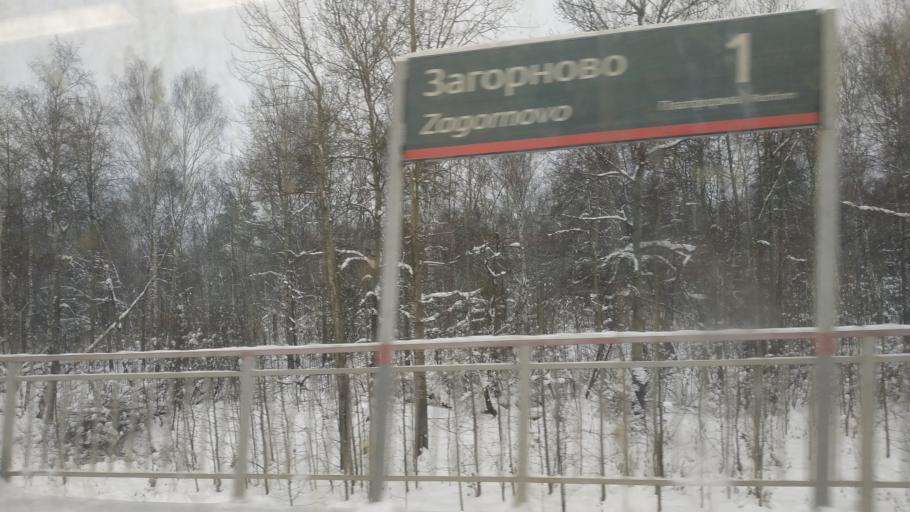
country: RU
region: Moskovskaya
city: Malyshevo
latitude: 55.5158
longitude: 38.3360
